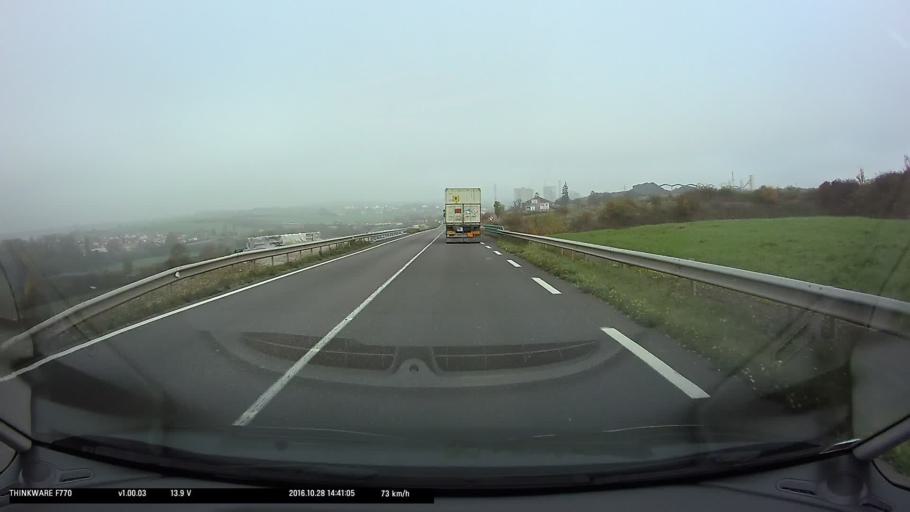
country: FR
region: Lorraine
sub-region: Departement de la Moselle
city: Lorquin
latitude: 48.6818
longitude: 6.9541
